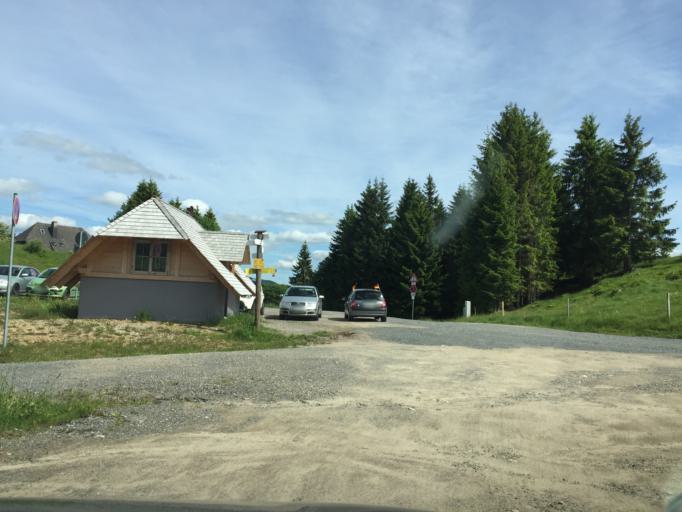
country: DE
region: Baden-Wuerttemberg
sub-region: Freiburg Region
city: Todtnau
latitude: 47.8593
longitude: 7.9396
